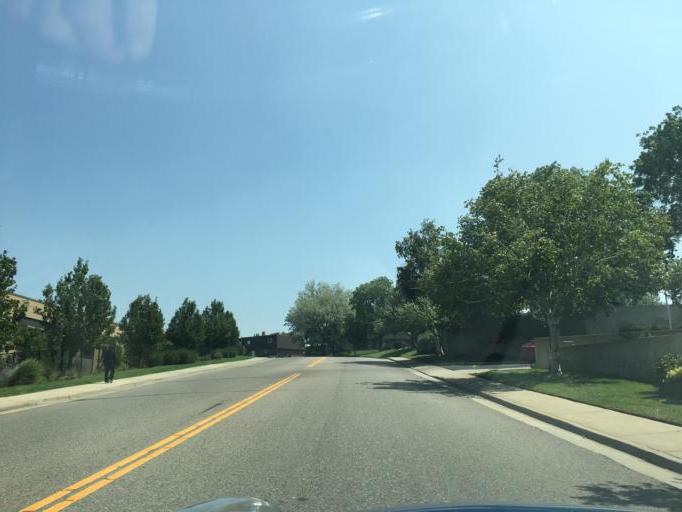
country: US
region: Colorado
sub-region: Jefferson County
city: West Pleasant View
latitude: 39.7219
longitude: -105.1645
